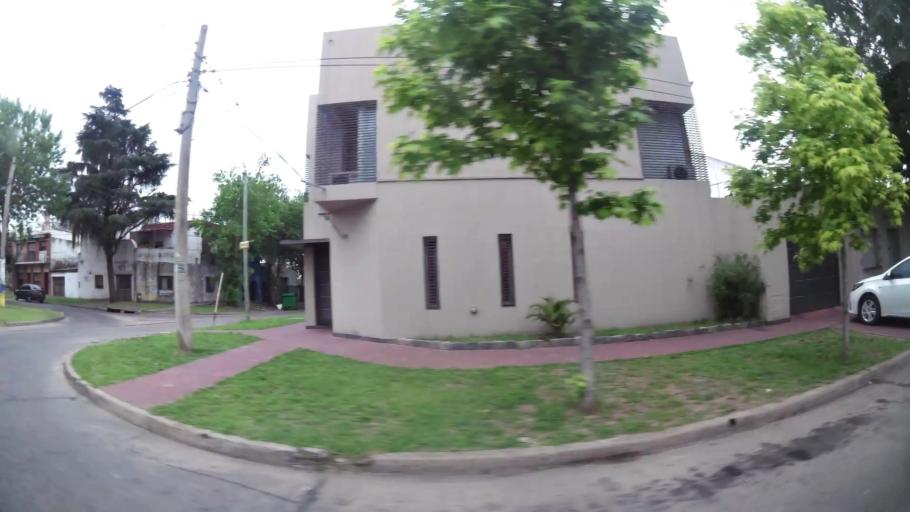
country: AR
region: Santa Fe
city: Granadero Baigorria
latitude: -32.9060
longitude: -60.6929
